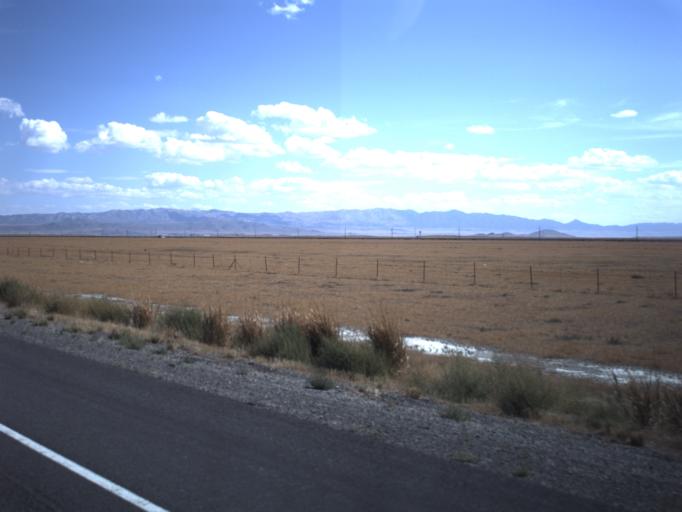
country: US
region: Utah
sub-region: Tooele County
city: Wendover
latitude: 40.7263
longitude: -113.2488
